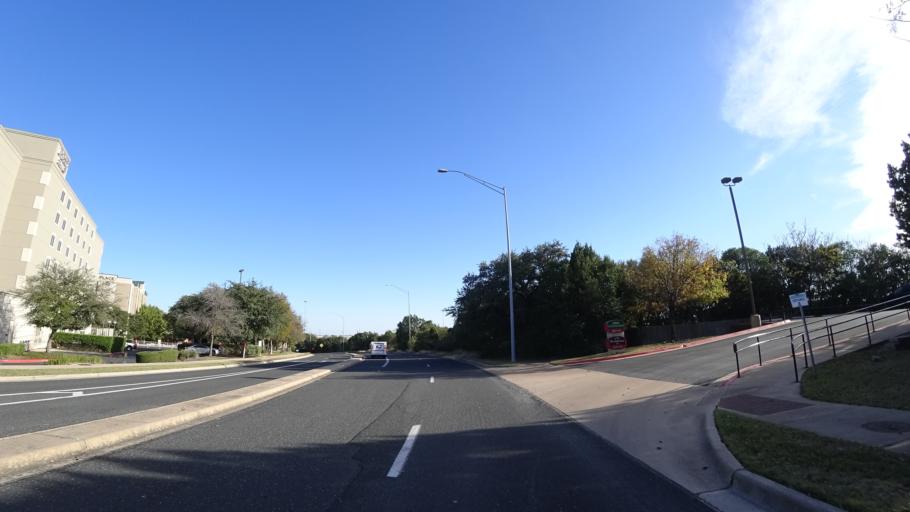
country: US
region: Texas
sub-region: Williamson County
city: Jollyville
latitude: 30.3850
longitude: -97.7392
